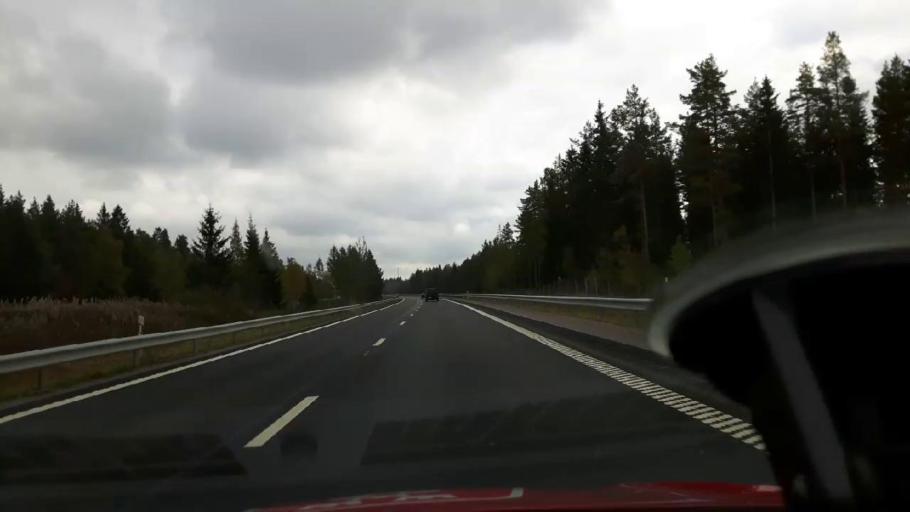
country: SE
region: Gaevleborg
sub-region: Gavle Kommun
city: Gavle
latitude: 60.6239
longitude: 17.1562
